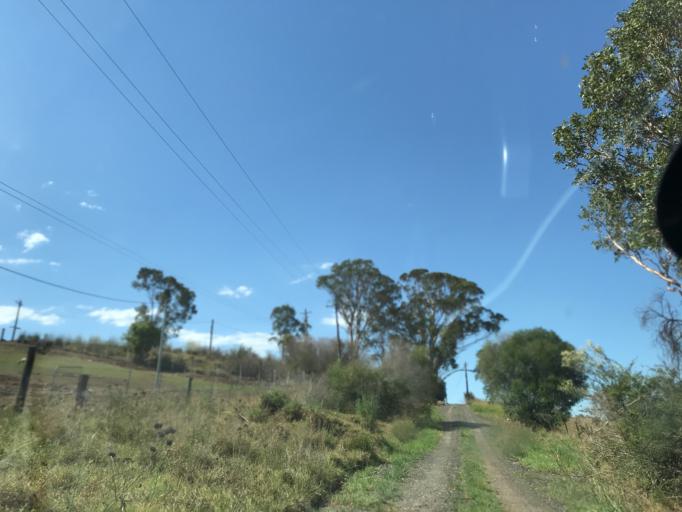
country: AU
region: New South Wales
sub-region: Penrith Municipality
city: Kingswood Park
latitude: -33.7938
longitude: 150.7374
